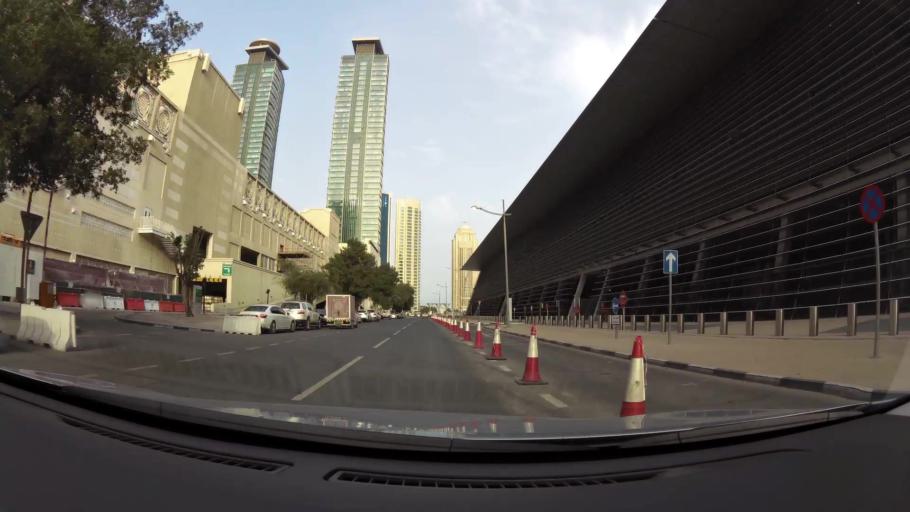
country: QA
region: Baladiyat ad Dawhah
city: Doha
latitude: 25.3242
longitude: 51.5303
